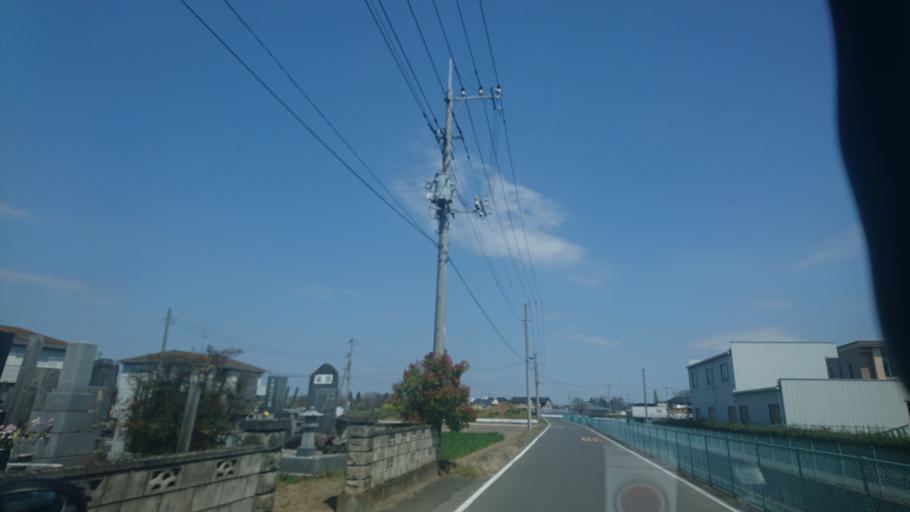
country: JP
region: Ibaraki
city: Ishige
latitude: 36.1512
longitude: 139.9641
